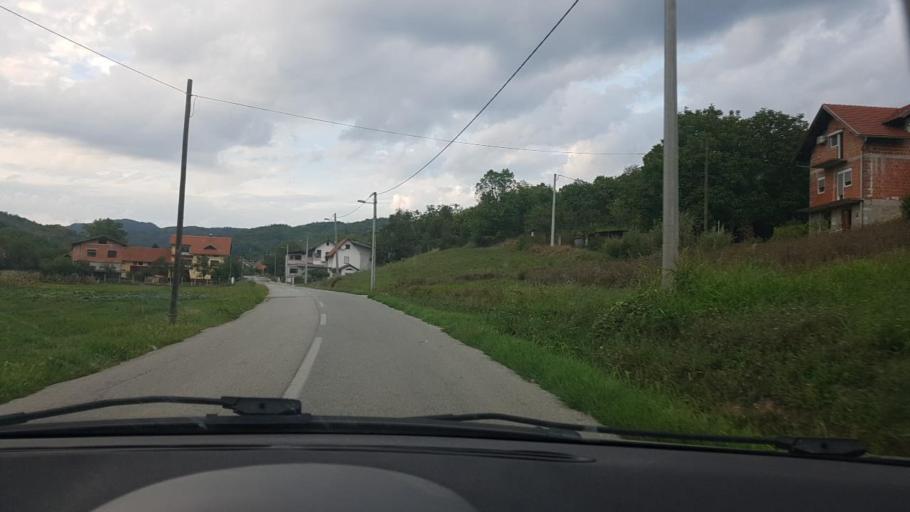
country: HR
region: Krapinsko-Zagorska
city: Marija Bistrica
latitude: 45.9277
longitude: 16.1715
